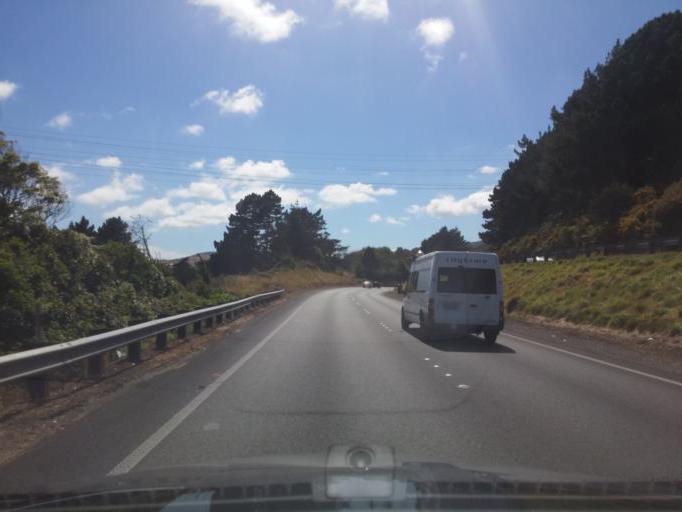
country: NZ
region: Wellington
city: Petone
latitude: -41.1966
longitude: 174.8254
